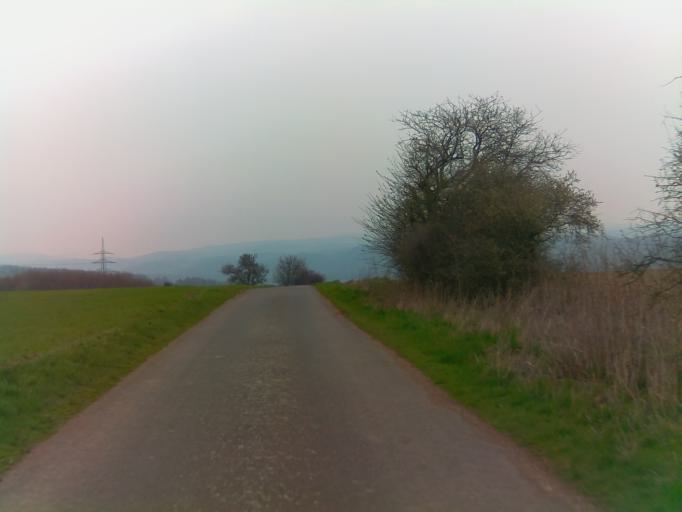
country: DE
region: Rheinland-Pfalz
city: Hoppstadten-Weiersbach
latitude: 49.6280
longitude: 7.2081
